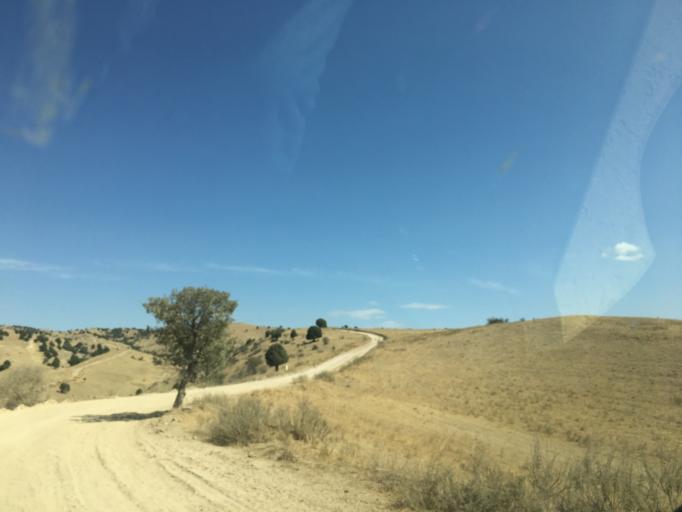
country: TM
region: Ahal
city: Baharly
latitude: 38.2960
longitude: 56.9360
